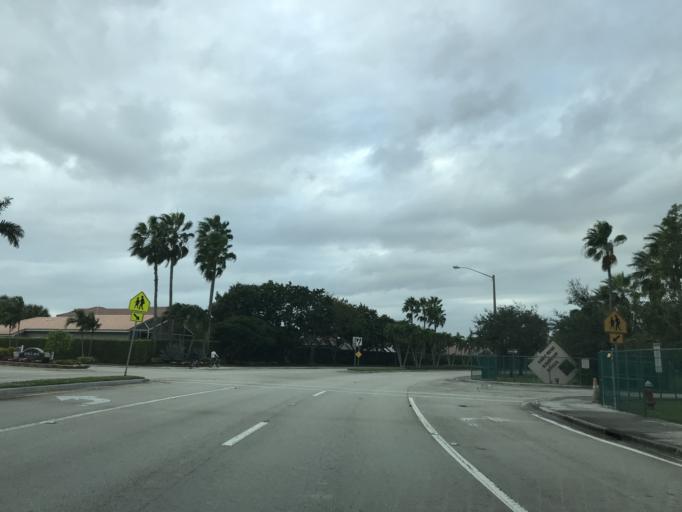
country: US
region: Florida
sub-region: Broward County
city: Coral Springs
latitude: 26.2960
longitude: -80.2823
